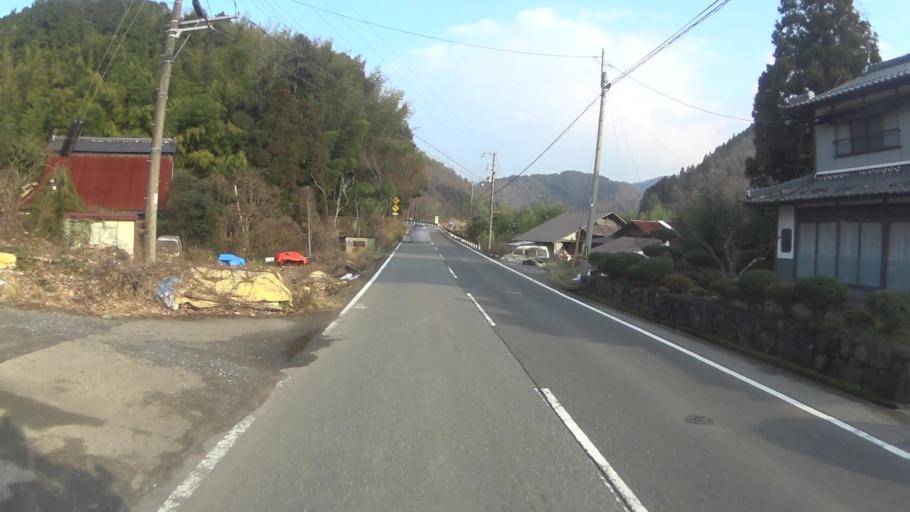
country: JP
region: Kyoto
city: Maizuru
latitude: 35.3681
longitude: 135.4243
